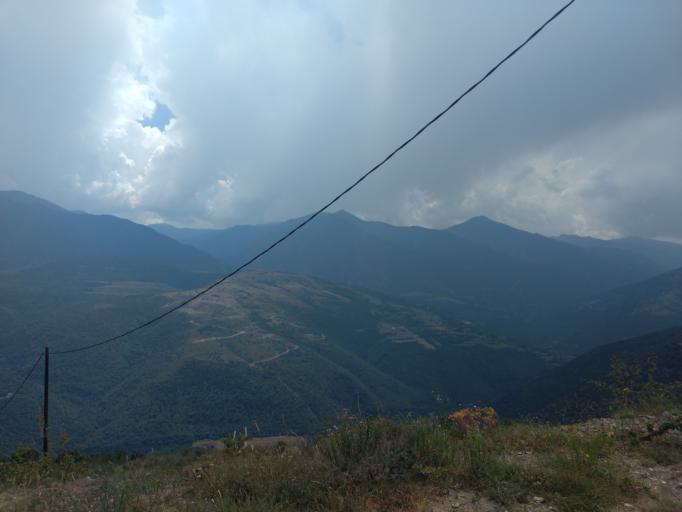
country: FR
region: Languedoc-Roussillon
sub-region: Departement des Pyrenees-Orientales
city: Vernet-les-Bains
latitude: 42.5726
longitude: 2.2921
